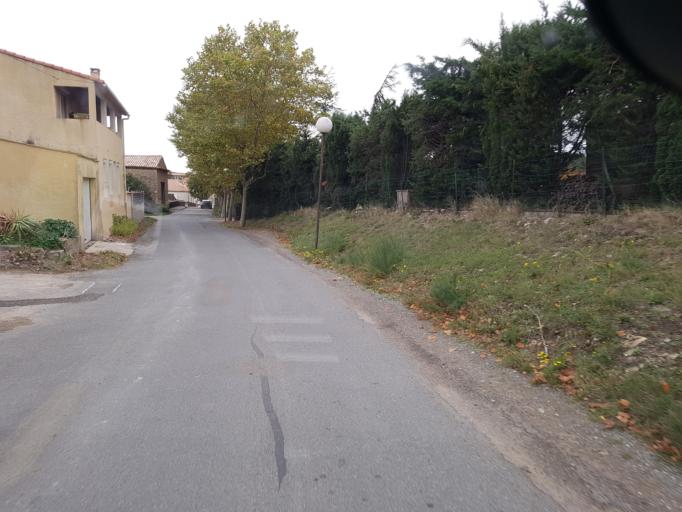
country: FR
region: Languedoc-Roussillon
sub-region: Departement de l'Aude
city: Conques-sur-Orbiel
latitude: 43.3138
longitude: 2.4587
